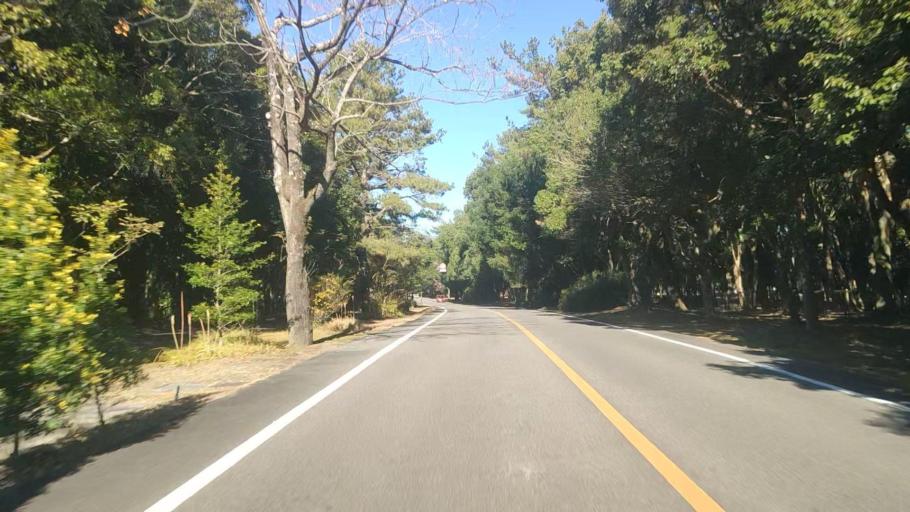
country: JP
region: Miyazaki
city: Miyazaki-shi
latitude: 31.9476
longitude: 131.4653
